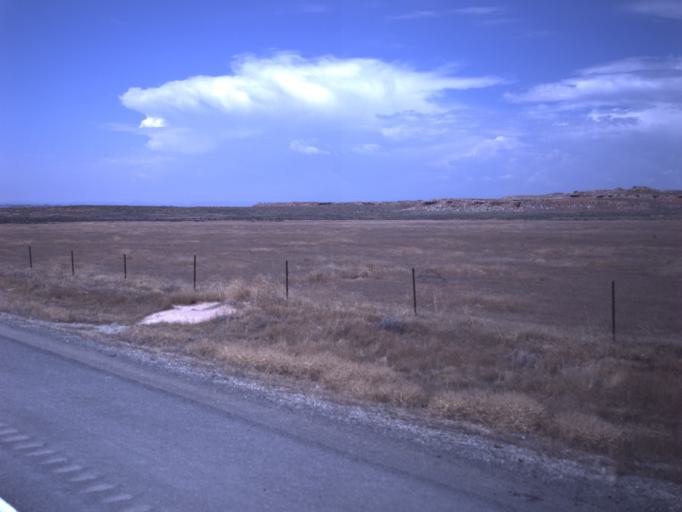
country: US
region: Utah
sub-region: Uintah County
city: Maeser
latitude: 40.3120
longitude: -109.7458
